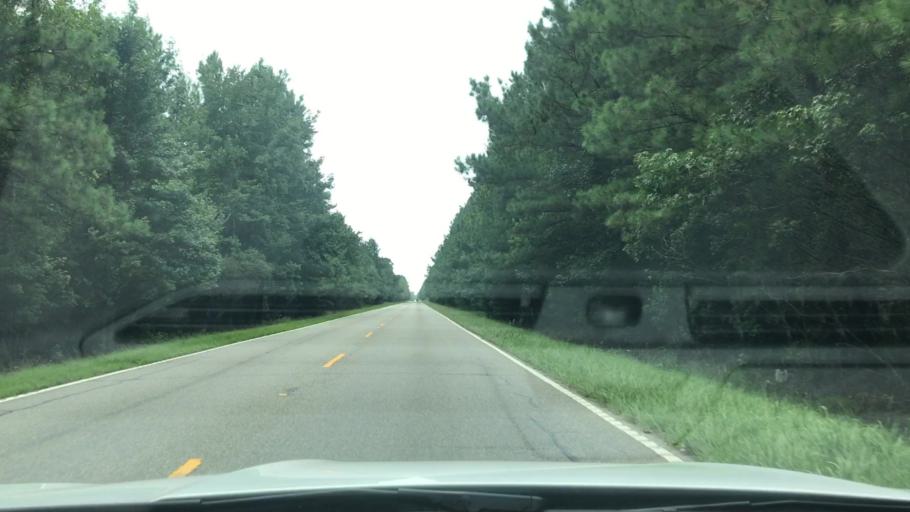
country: US
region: South Carolina
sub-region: Georgetown County
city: Murrells Inlet
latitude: 33.5494
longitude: -79.2217
